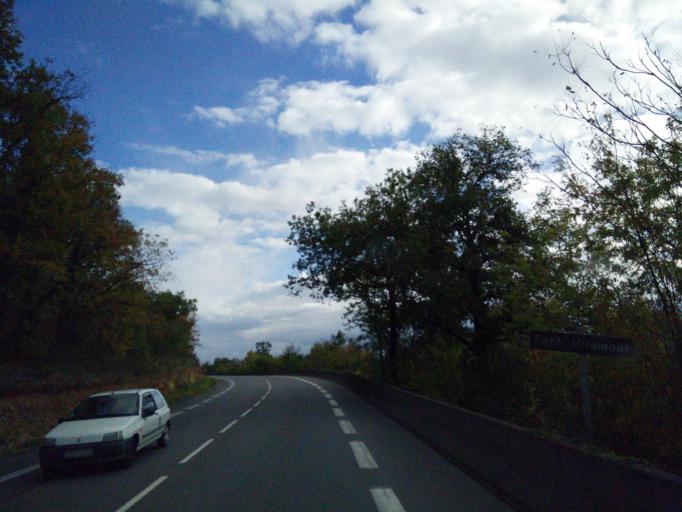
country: FR
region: Midi-Pyrenees
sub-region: Departement du Lot
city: Pradines
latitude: 44.4833
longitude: 1.4104
